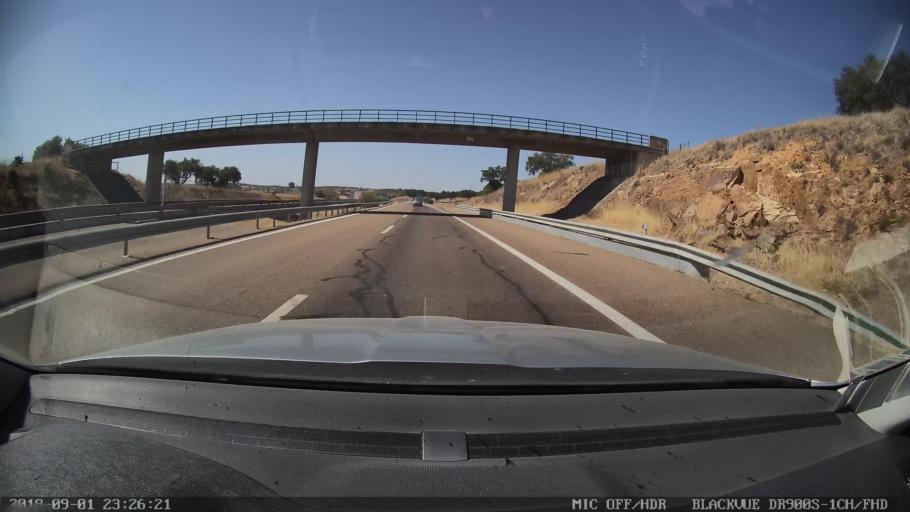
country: PT
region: Portalegre
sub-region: Elvas
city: Elvas
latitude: 38.8982
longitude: -7.2026
